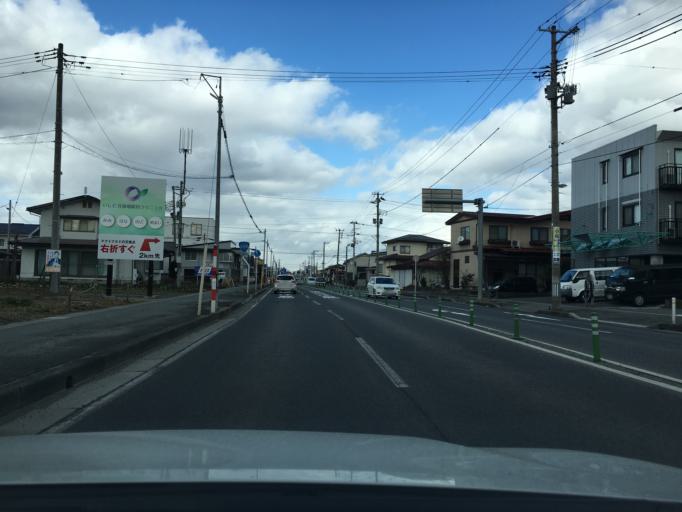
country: JP
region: Yamagata
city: Yamagata-shi
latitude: 38.2334
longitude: 140.3054
